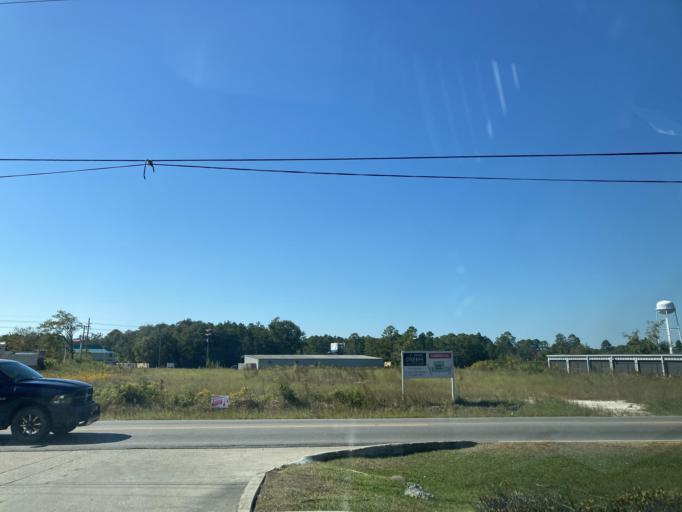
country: US
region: Mississippi
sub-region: Jackson County
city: Gulf Hills
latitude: 30.4586
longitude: -88.8417
